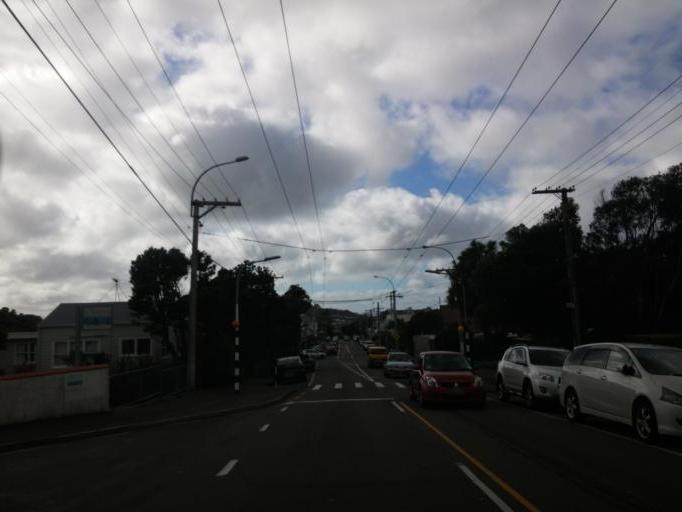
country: NZ
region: Wellington
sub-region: Wellington City
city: Kelburn
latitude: -41.2829
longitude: 174.7438
